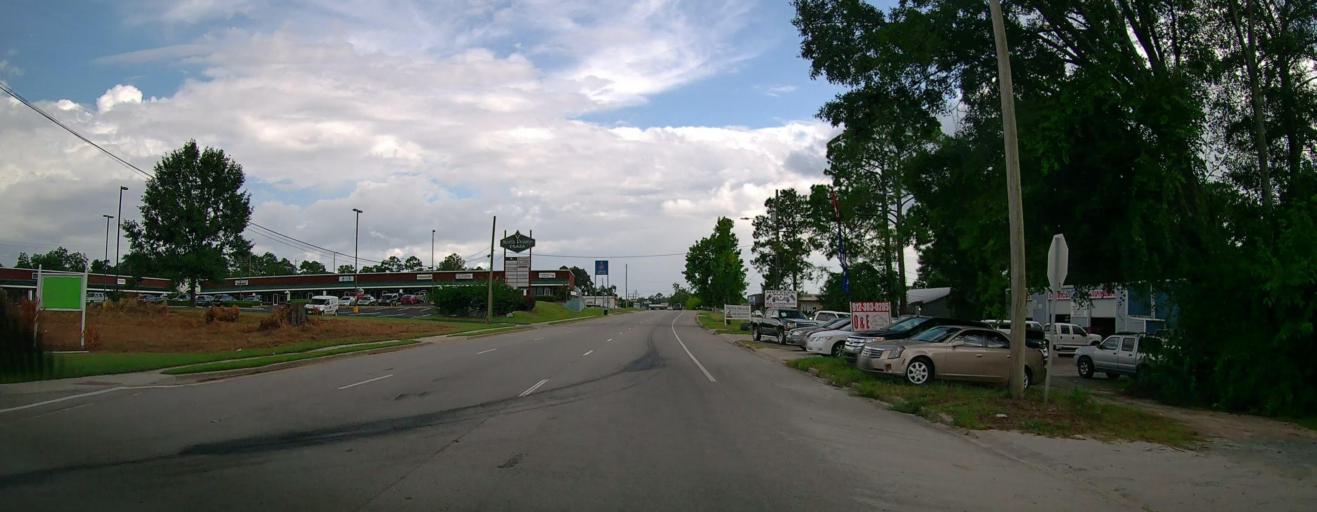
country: US
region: Georgia
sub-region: Coffee County
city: Douglas
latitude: 31.5233
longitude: -82.8505
